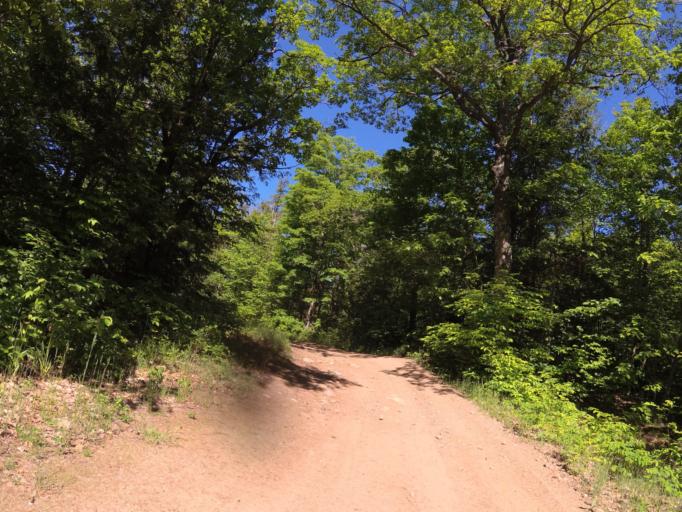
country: CA
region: Ontario
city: Renfrew
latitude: 45.0929
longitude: -77.0759
